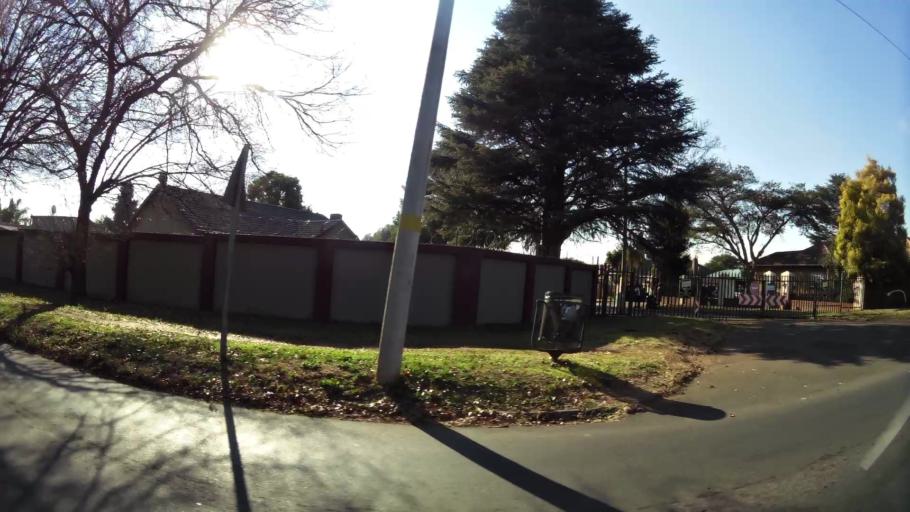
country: ZA
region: Gauteng
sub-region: City of Johannesburg Metropolitan Municipality
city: Modderfontein
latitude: -26.1478
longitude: 28.1636
